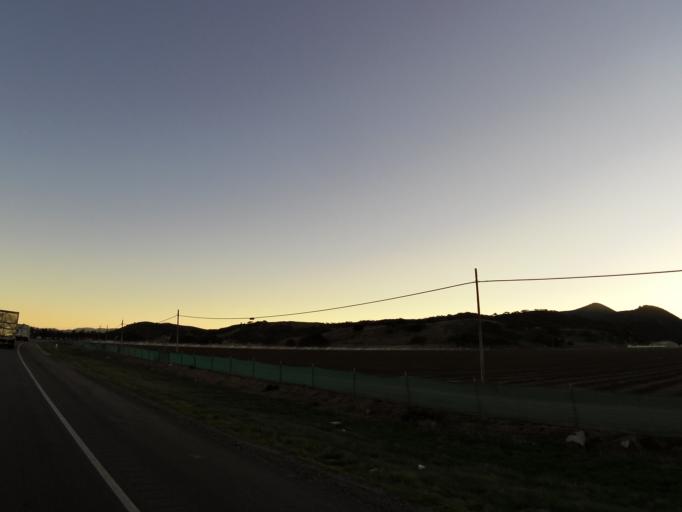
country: US
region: California
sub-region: Monterey County
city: King City
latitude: 36.2228
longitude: -121.1699
